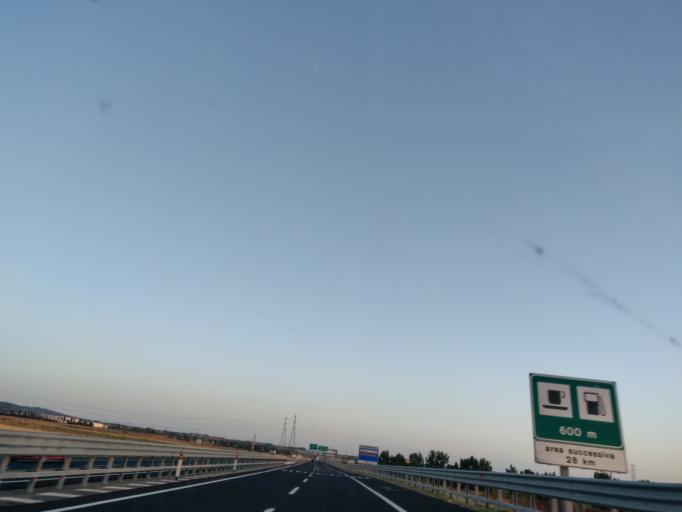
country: IT
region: Latium
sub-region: Citta metropolitana di Roma Capitale
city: Aurelia
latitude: 42.1762
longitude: 11.7900
